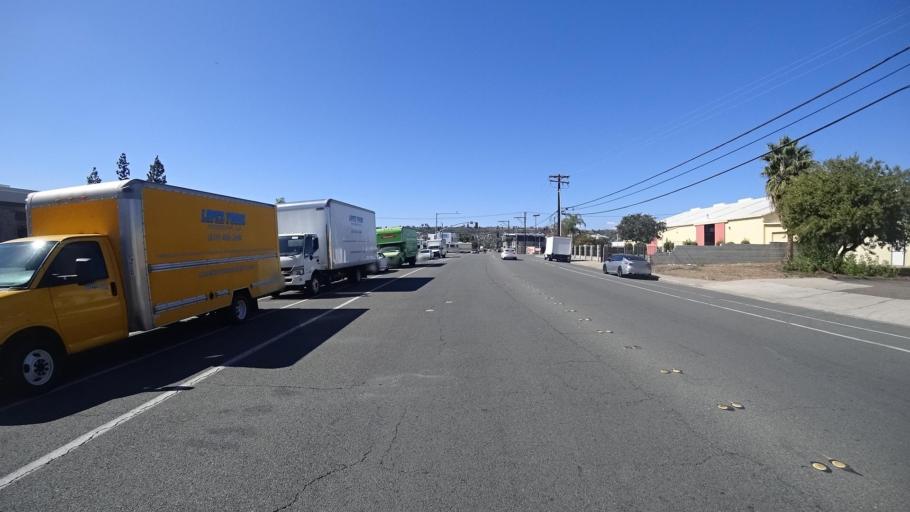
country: US
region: California
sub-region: San Diego County
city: El Cajon
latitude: 32.8123
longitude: -116.9667
